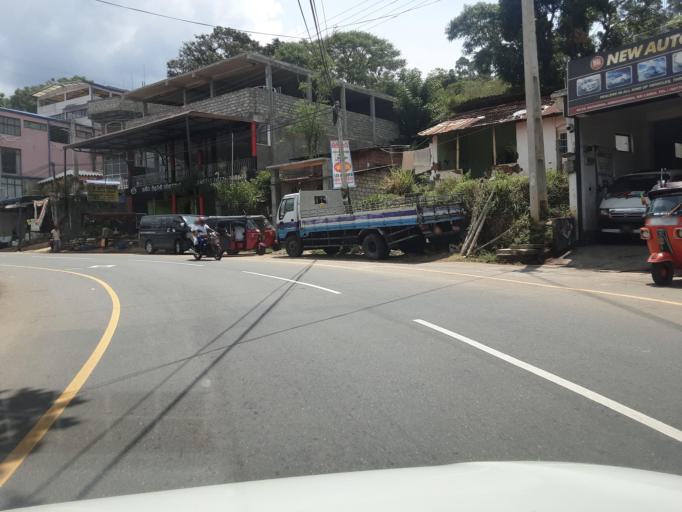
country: LK
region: Central
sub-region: Nuwara Eliya District
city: Nuwara Eliya
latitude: 6.9219
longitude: 80.9006
